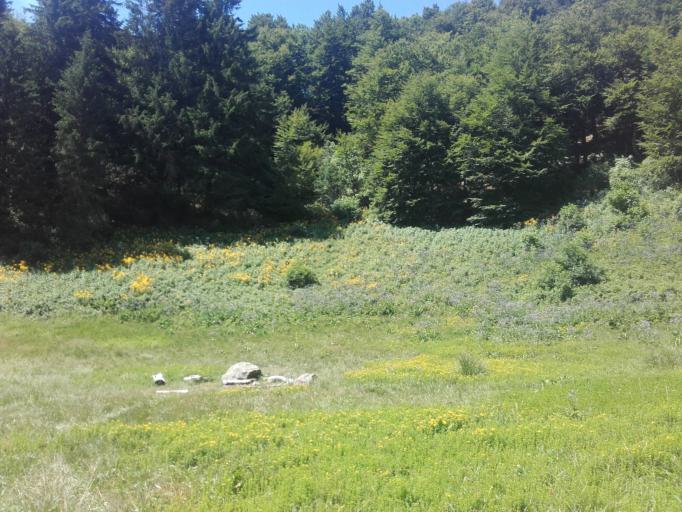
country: FR
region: Auvergne
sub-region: Departement du Puy-de-Dome
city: Mont-Dore
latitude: 45.4874
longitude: 2.8854
